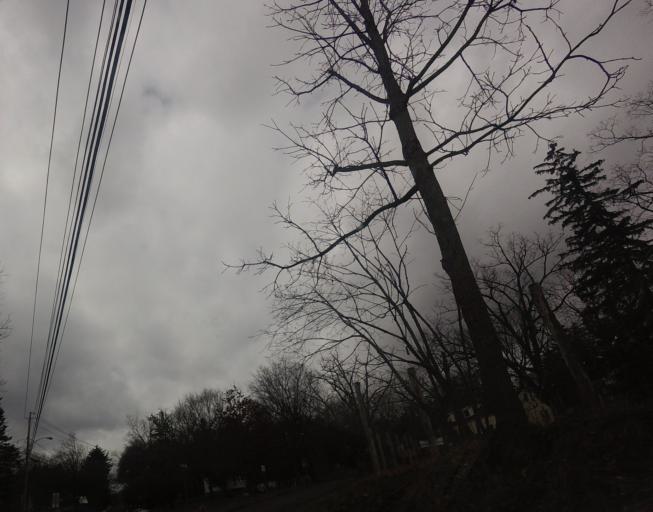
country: US
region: New York
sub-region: Tompkins County
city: Ithaca
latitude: 42.4384
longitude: -76.5187
